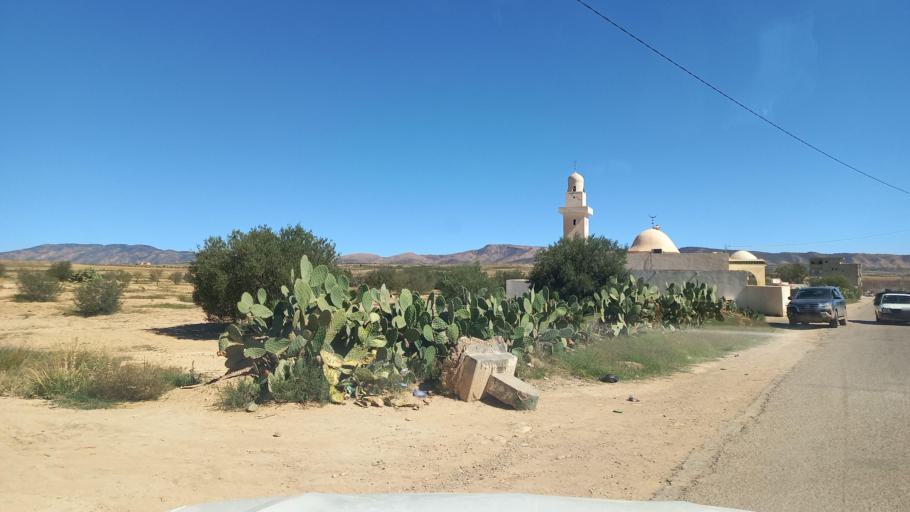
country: TN
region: Al Qasrayn
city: Sbiba
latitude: 35.3636
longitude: 9.0884
